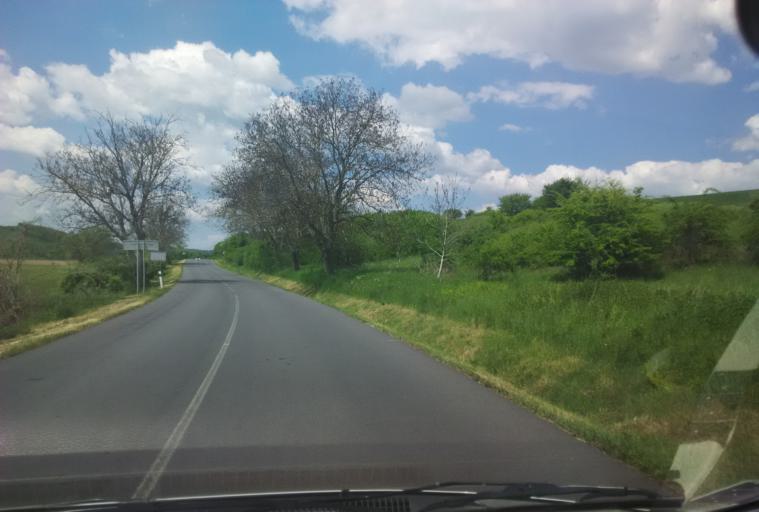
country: SK
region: Banskobystricky
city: Dudince
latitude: 48.1695
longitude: 18.8645
